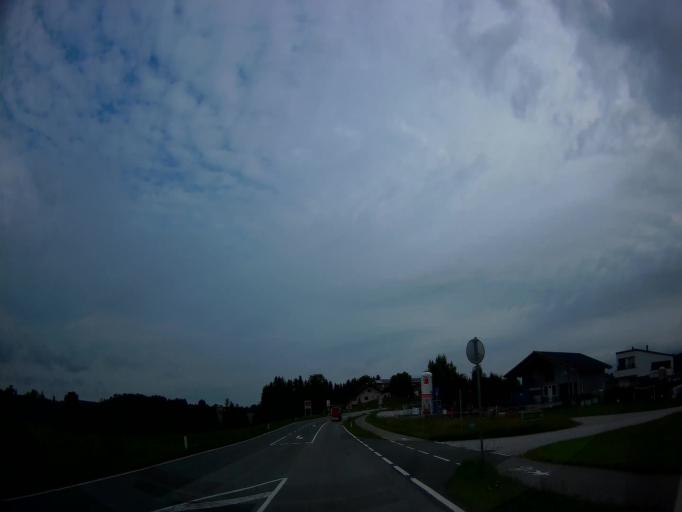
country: AT
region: Salzburg
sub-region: Politischer Bezirk Salzburg-Umgebung
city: Mattsee
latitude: 47.9941
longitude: 13.1175
